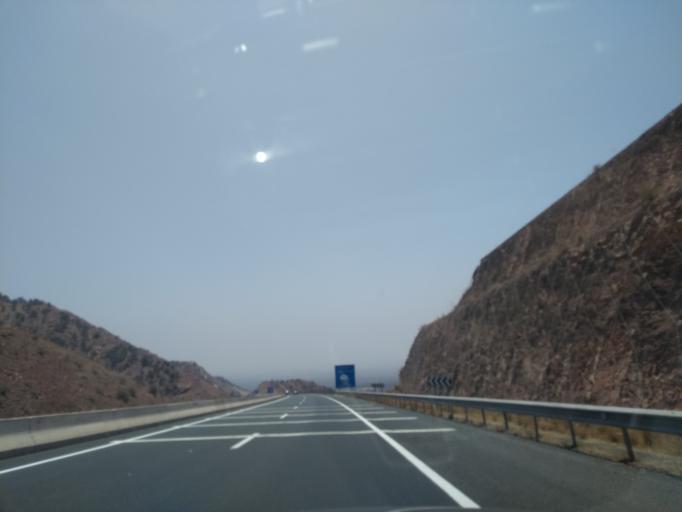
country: MA
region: Souss-Massa-Draa
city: Oulad Teima
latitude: 30.5554
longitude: -9.3351
